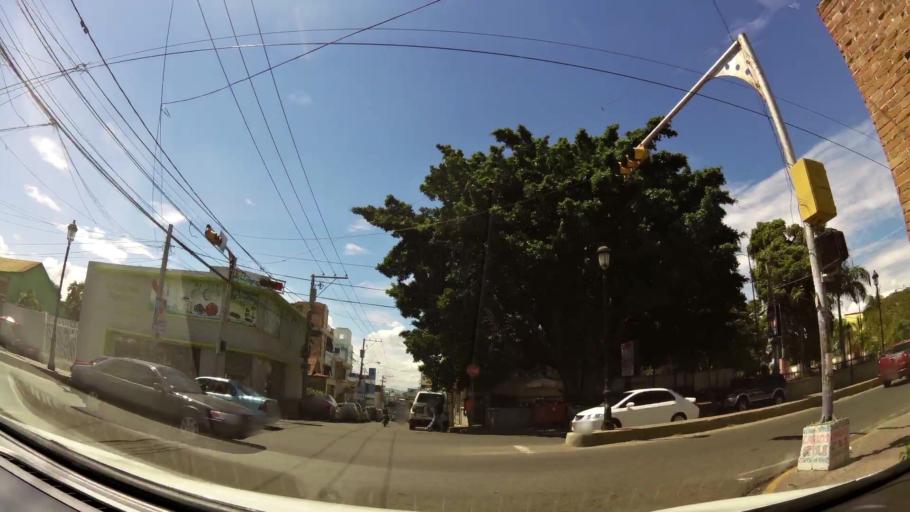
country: DO
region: Santiago
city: Santiago de los Caballeros
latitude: 19.4532
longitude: -70.7073
